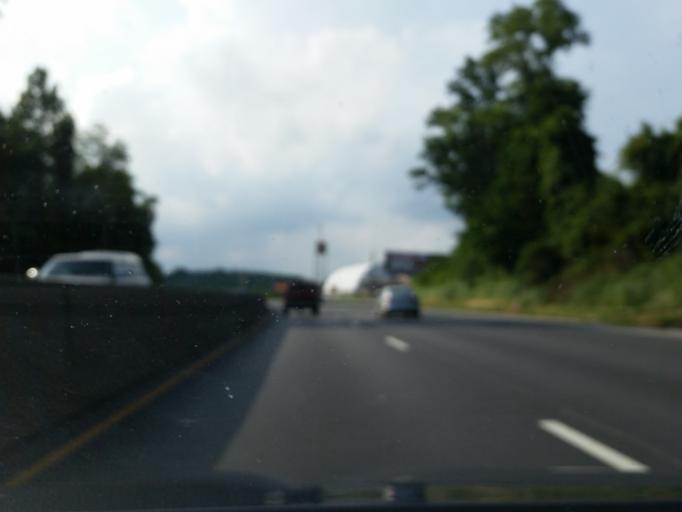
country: US
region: Pennsylvania
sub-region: York County
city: Valley Green
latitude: 40.1278
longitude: -76.7927
